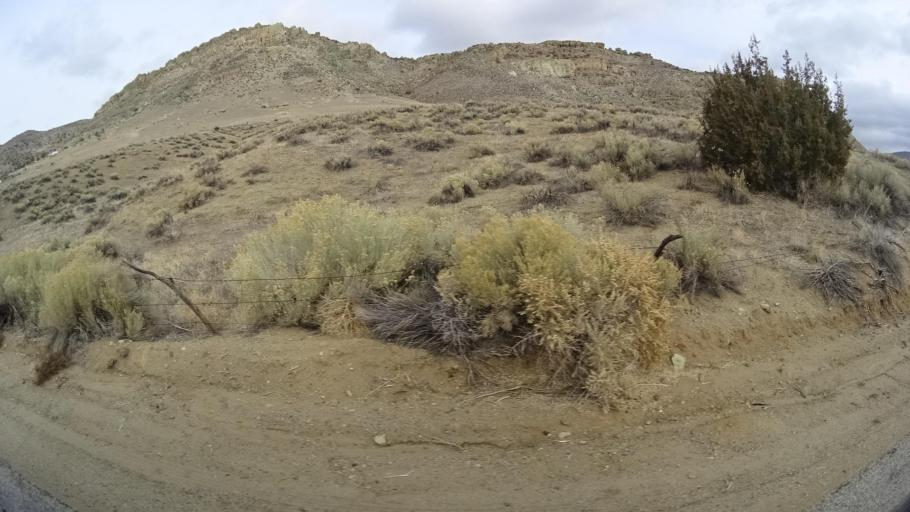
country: US
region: California
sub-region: Kern County
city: Tehachapi
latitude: 35.1370
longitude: -118.3209
